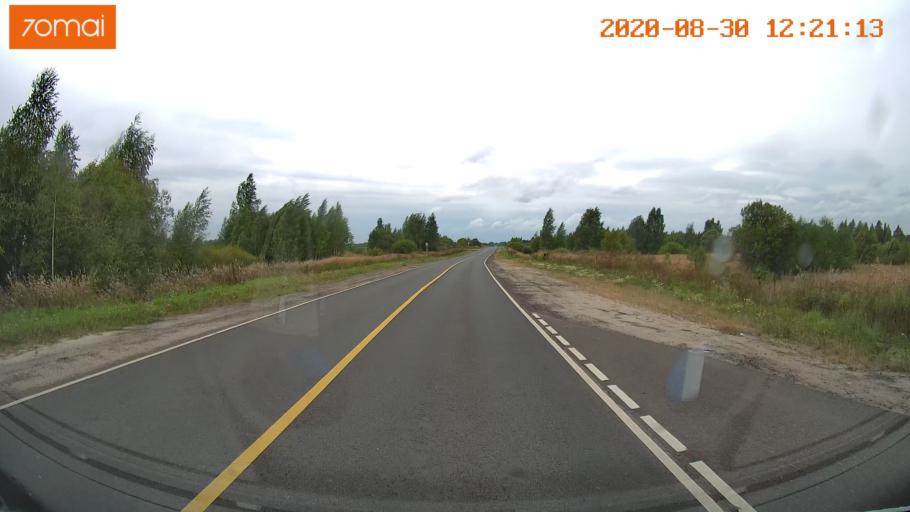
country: RU
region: Ivanovo
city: Yur'yevets
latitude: 57.3243
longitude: 42.8807
